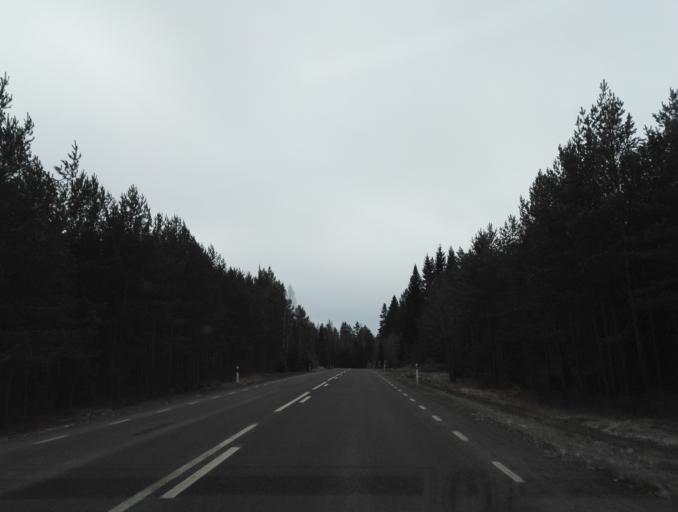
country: SE
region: Kalmar
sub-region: Hultsfreds Kommun
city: Virserum
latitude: 57.3389
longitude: 15.6032
